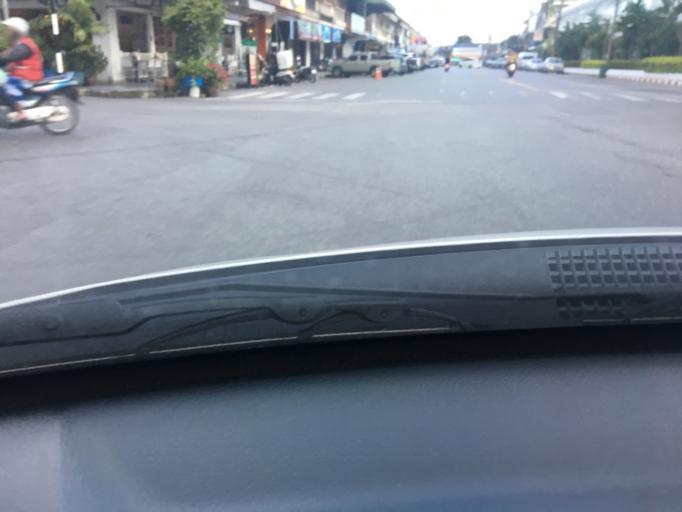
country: TH
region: Phuket
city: Ban Talat Yai
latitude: 7.8800
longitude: 98.3955
